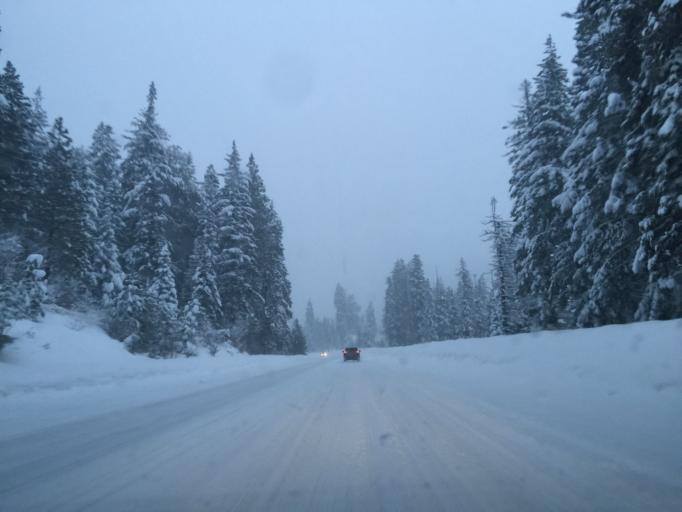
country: US
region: Washington
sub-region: Chelan County
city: Leavenworth
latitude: 47.7828
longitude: -120.8998
